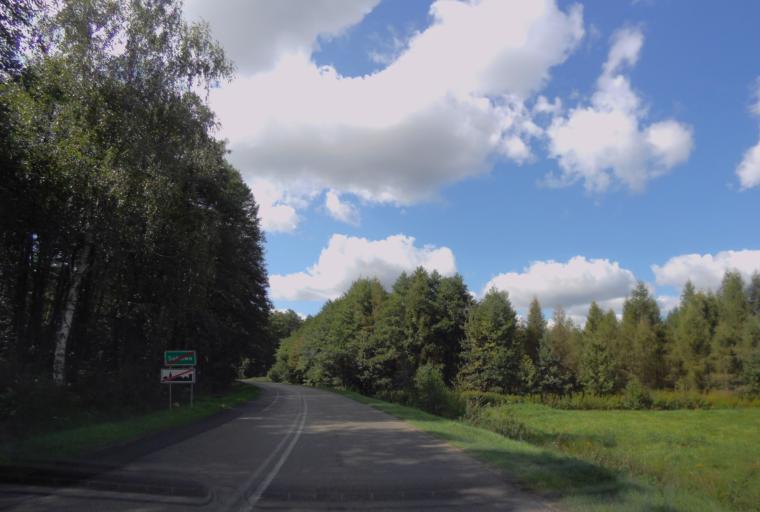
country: PL
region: Subcarpathian Voivodeship
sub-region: Powiat stalowowolski
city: Bojanow
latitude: 50.4024
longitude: 22.0343
